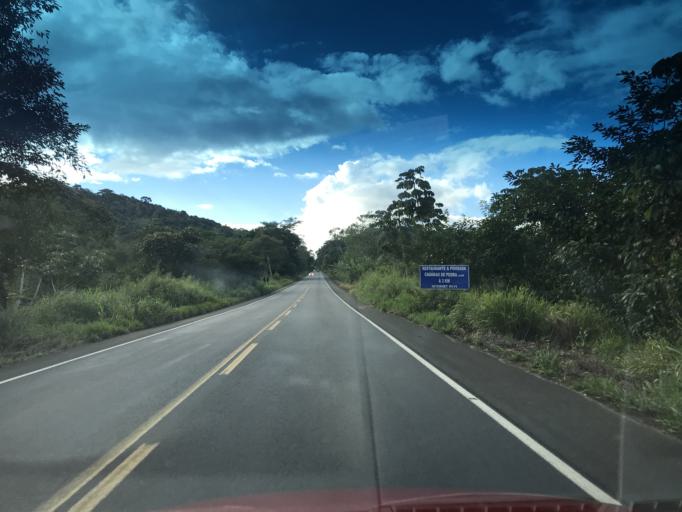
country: BR
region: Bahia
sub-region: Ibirapitanga
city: Ibirapitanga
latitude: -14.1961
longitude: -39.3142
